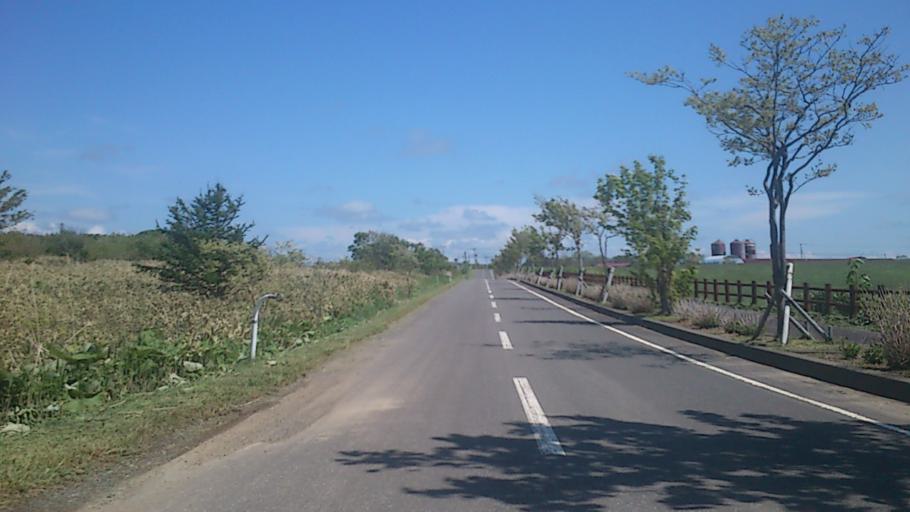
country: JP
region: Hokkaido
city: Rumoi
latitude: 44.5595
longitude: 141.7798
